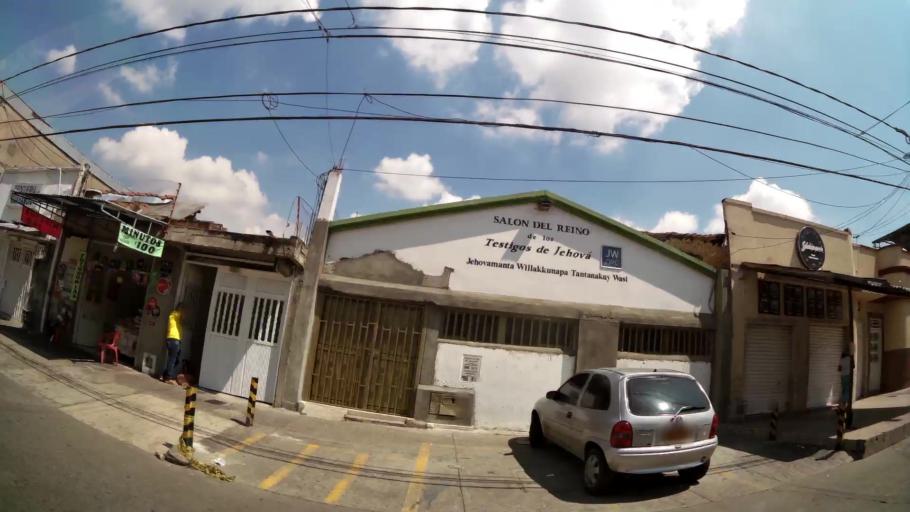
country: CO
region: Valle del Cauca
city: Cali
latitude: 3.4399
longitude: -76.5257
